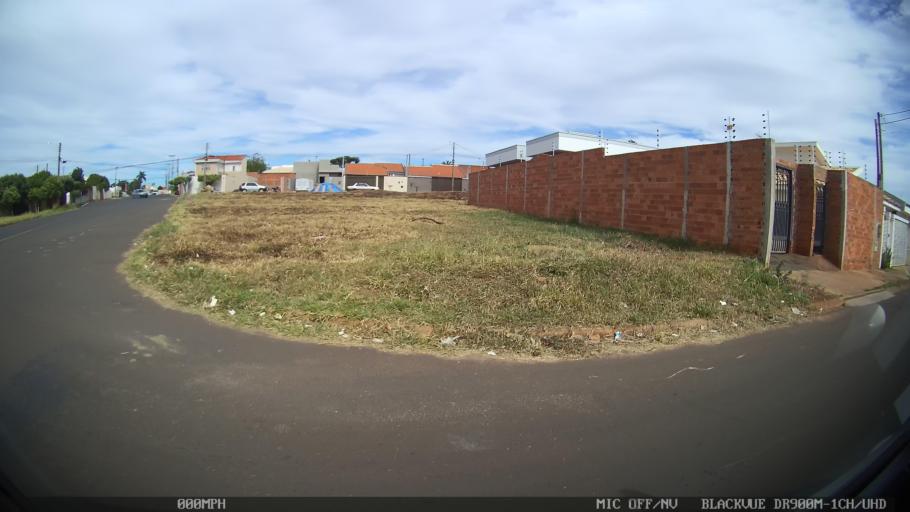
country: BR
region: Sao Paulo
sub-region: Catanduva
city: Catanduva
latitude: -21.1593
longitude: -48.9702
